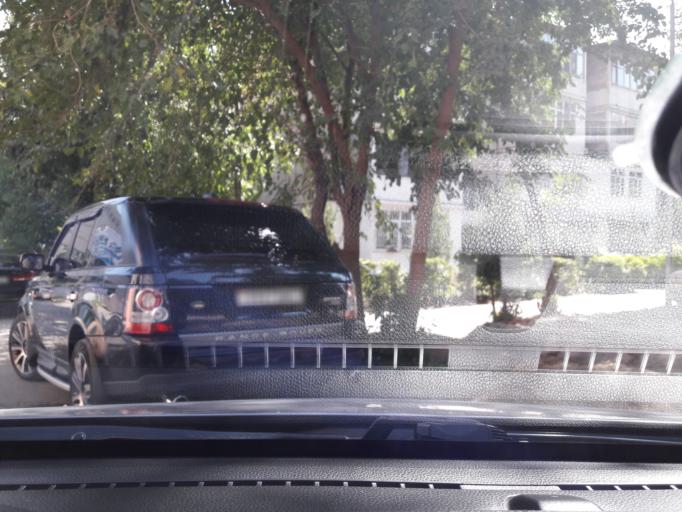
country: TJ
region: Dushanbe
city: Dushanbe
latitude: 38.5864
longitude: 68.7539
